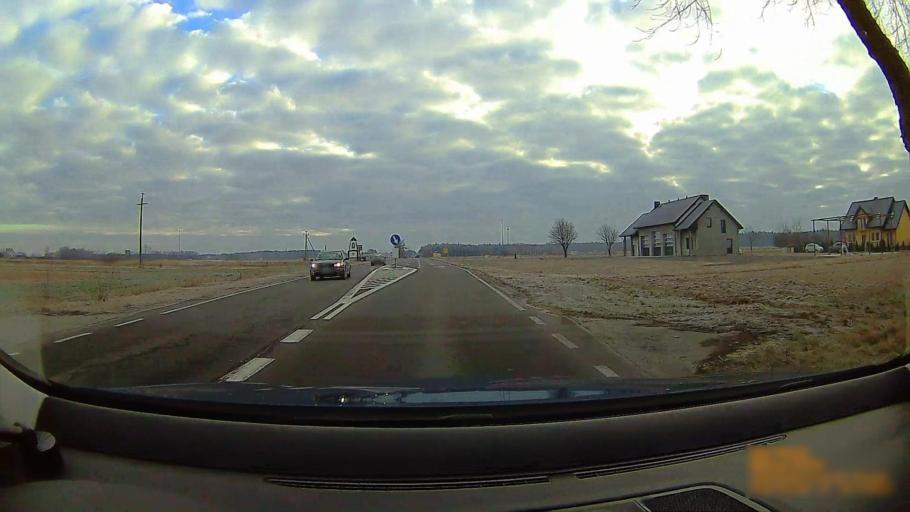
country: PL
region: Greater Poland Voivodeship
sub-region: Powiat koninski
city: Stare Miasto
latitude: 52.2010
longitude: 18.1909
